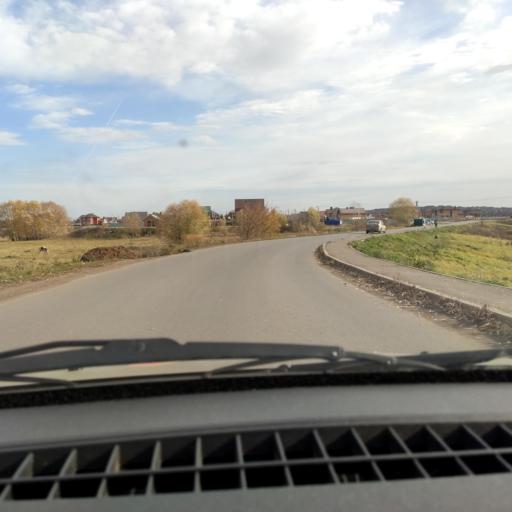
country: RU
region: Bashkortostan
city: Ufa
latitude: 54.6101
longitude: 55.9039
